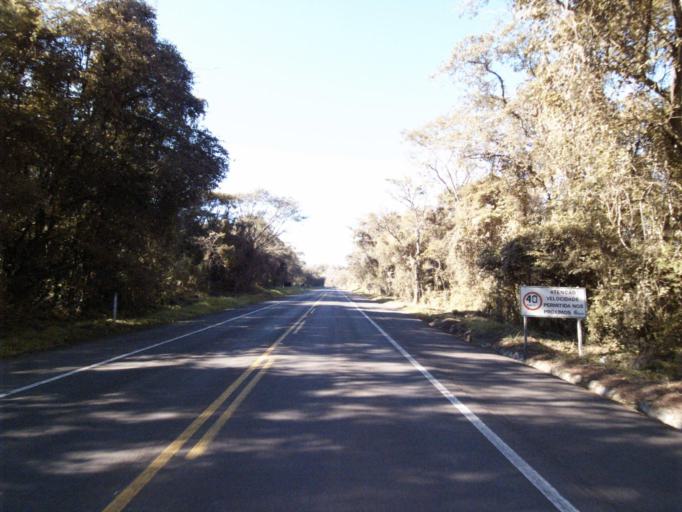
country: BR
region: Rio Grande do Sul
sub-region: Frederico Westphalen
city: Frederico Westphalen
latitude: -26.8091
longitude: -53.4397
